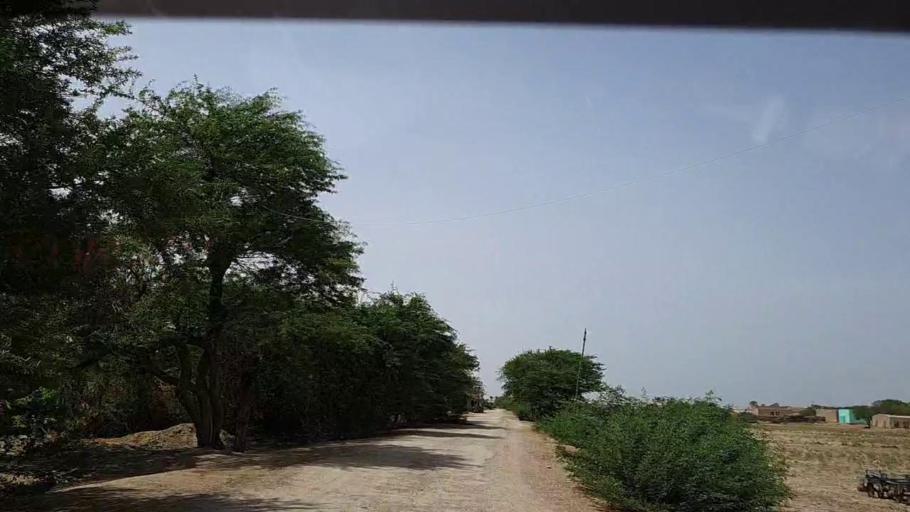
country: PK
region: Sindh
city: Johi
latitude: 26.7822
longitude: 67.6201
